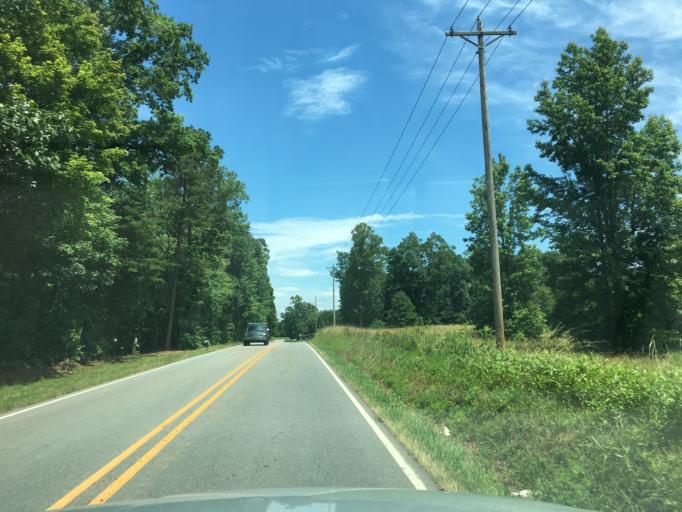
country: US
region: North Carolina
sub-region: Burke County
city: Glen Alpine
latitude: 35.6413
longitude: -81.7932
